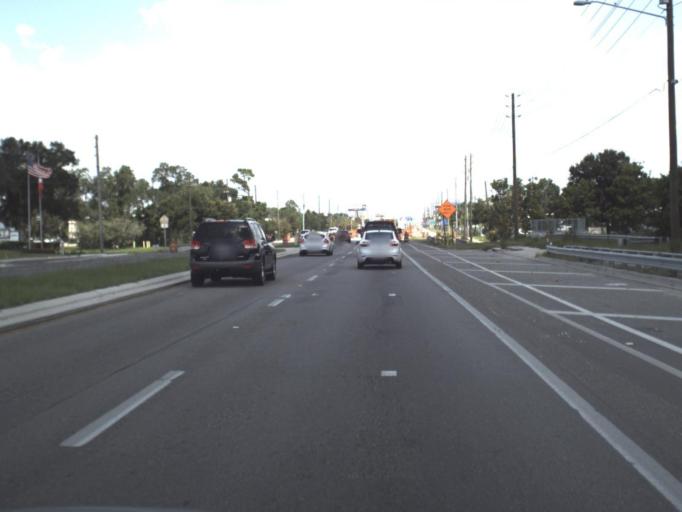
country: US
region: Florida
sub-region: Pinellas County
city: Largo
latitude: 27.8945
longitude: -82.7780
